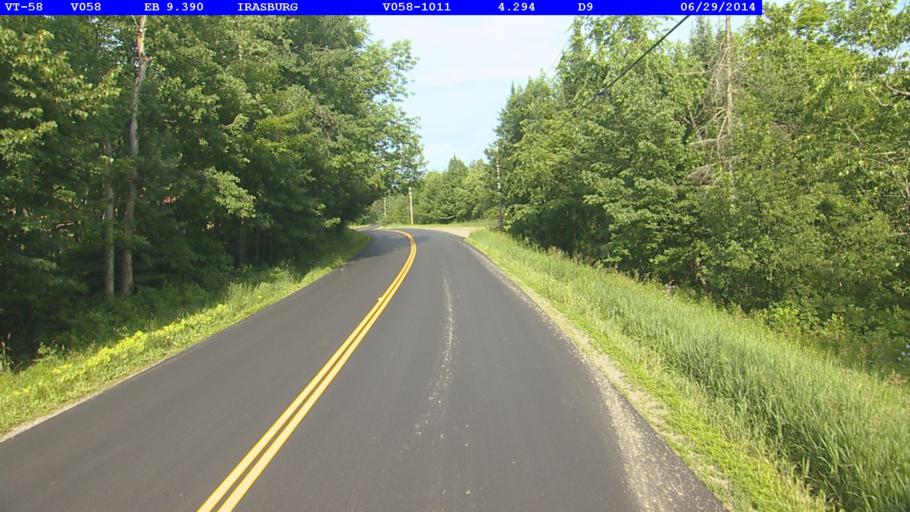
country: US
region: Vermont
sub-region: Orleans County
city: Newport
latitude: 44.8037
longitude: -72.2594
